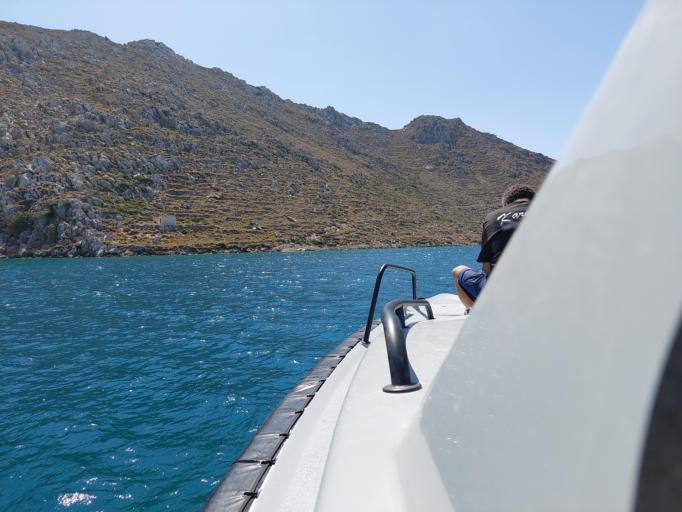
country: GR
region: South Aegean
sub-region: Nomos Dodekanisou
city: Karpathos
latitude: 35.8220
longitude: 27.2207
